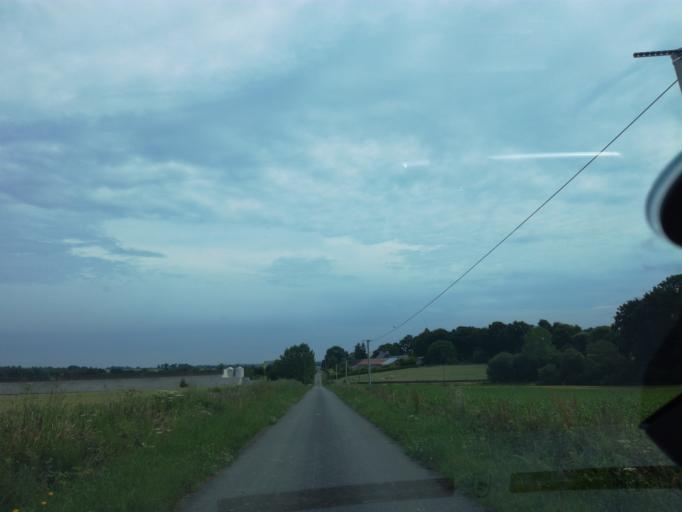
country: FR
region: Brittany
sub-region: Departement du Morbihan
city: Saint-Thuriau
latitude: 48.0156
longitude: -2.9174
